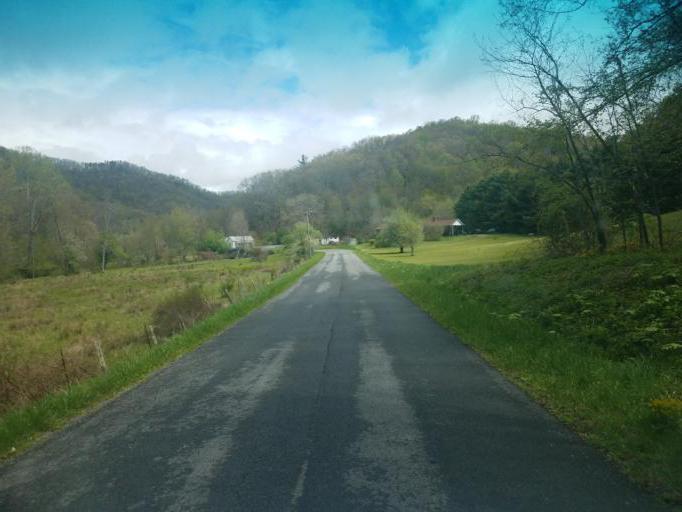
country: US
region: Virginia
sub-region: Smyth County
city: Atkins
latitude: 36.9831
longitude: -81.3954
